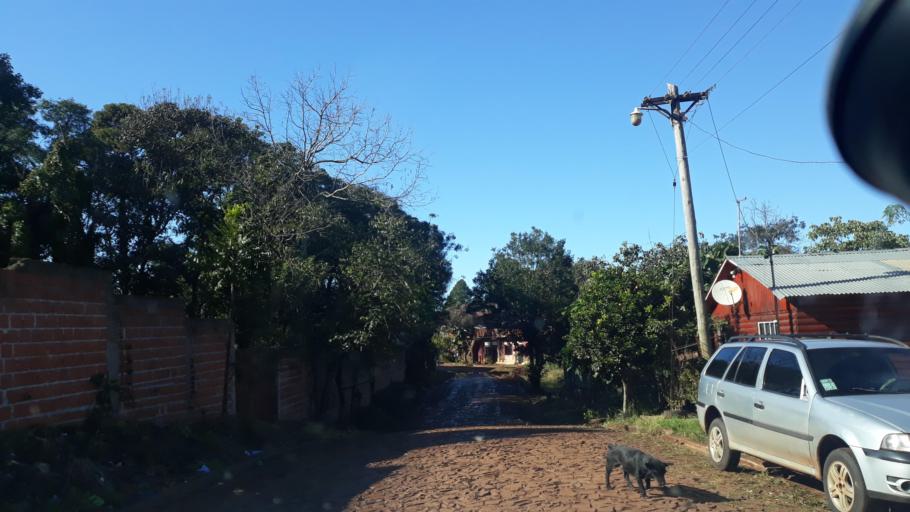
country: AR
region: Misiones
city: Bernardo de Irigoyen
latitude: -26.2591
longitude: -53.6486
